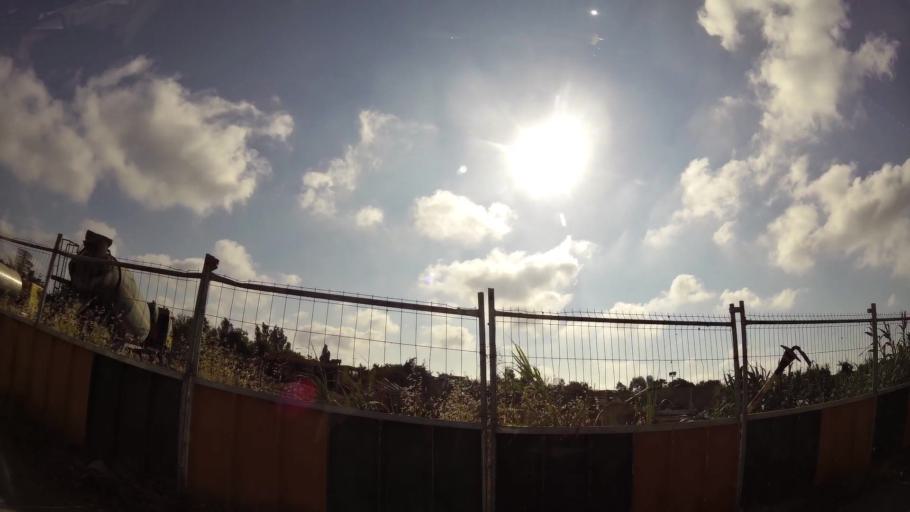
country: MA
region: Rabat-Sale-Zemmour-Zaer
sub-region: Rabat
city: Rabat
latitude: 33.9551
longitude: -6.8500
